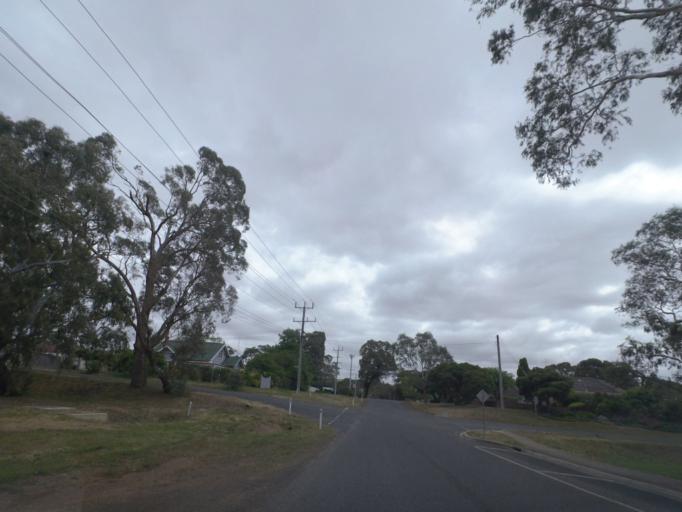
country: AU
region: Victoria
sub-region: Whittlesea
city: Whittlesea
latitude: -37.2028
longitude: 145.0430
